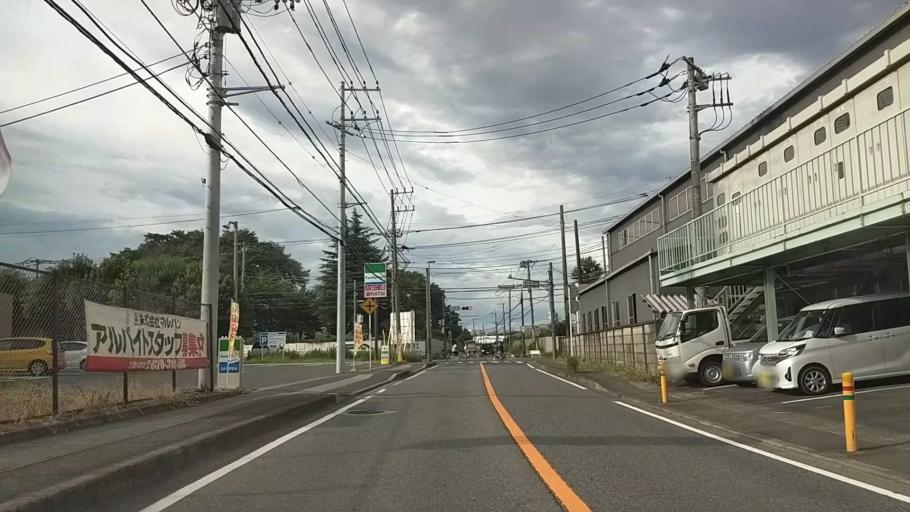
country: JP
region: Kanagawa
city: Zama
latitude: 35.5608
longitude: 139.3394
